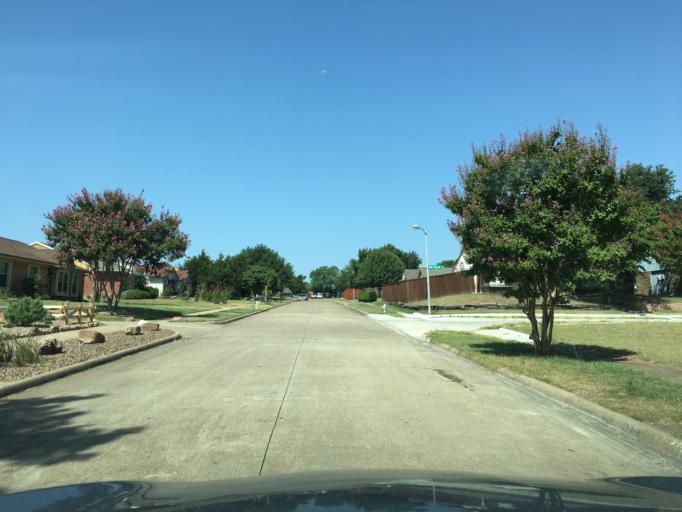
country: US
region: Texas
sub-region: Dallas County
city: Garland
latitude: 32.8878
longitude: -96.6150
